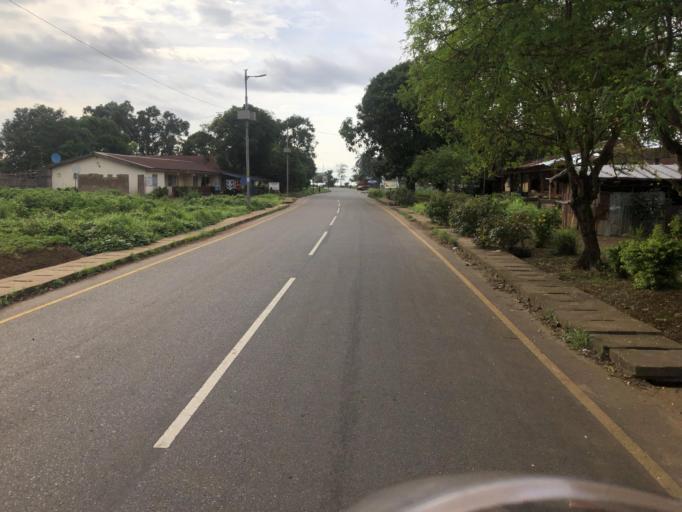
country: SL
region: Northern Province
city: Port Loko
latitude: 8.7742
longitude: -12.7928
